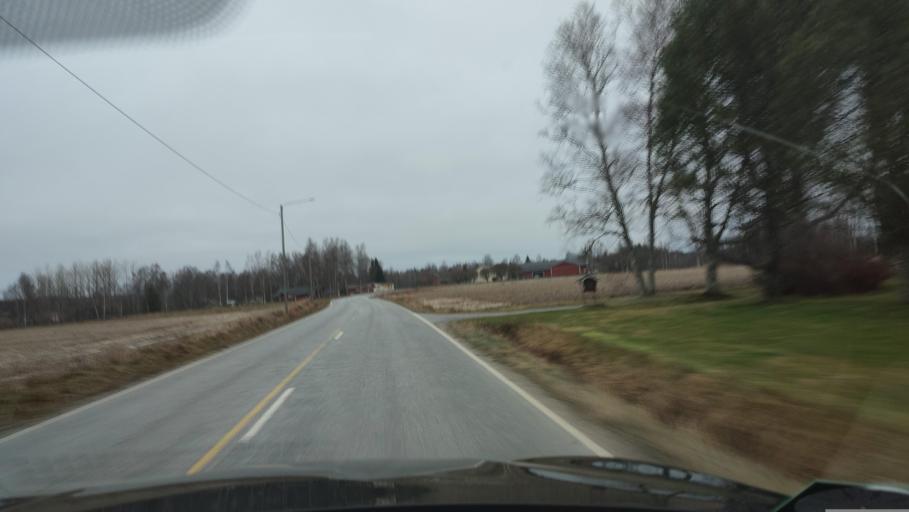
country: FI
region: Southern Ostrobothnia
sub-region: Suupohja
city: Karijoki
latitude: 62.2738
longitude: 21.7076
